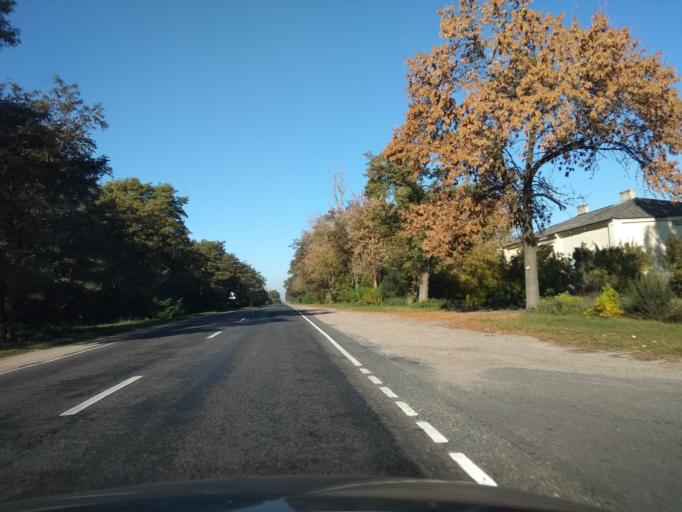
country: BY
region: Brest
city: Malaryta
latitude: 51.9288
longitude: 24.0655
